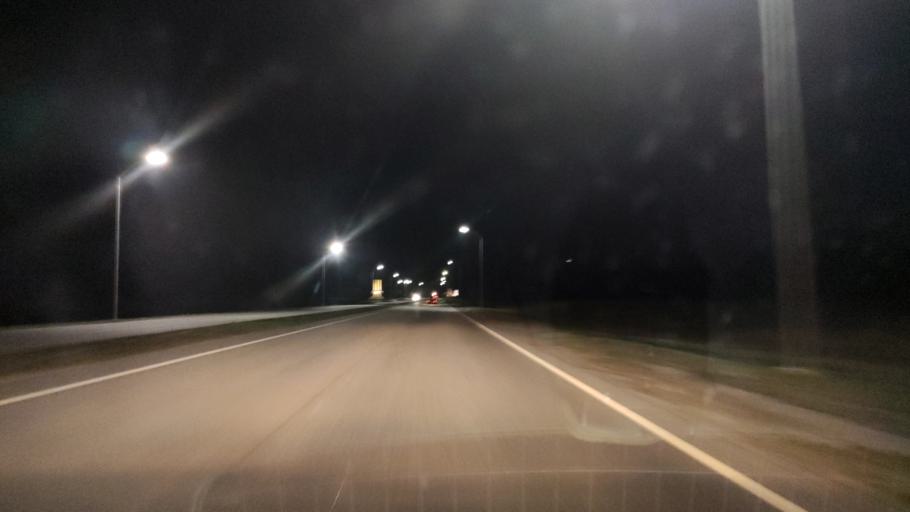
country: RU
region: Belgorod
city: Staryy Oskol
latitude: 51.4244
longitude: 37.8945
